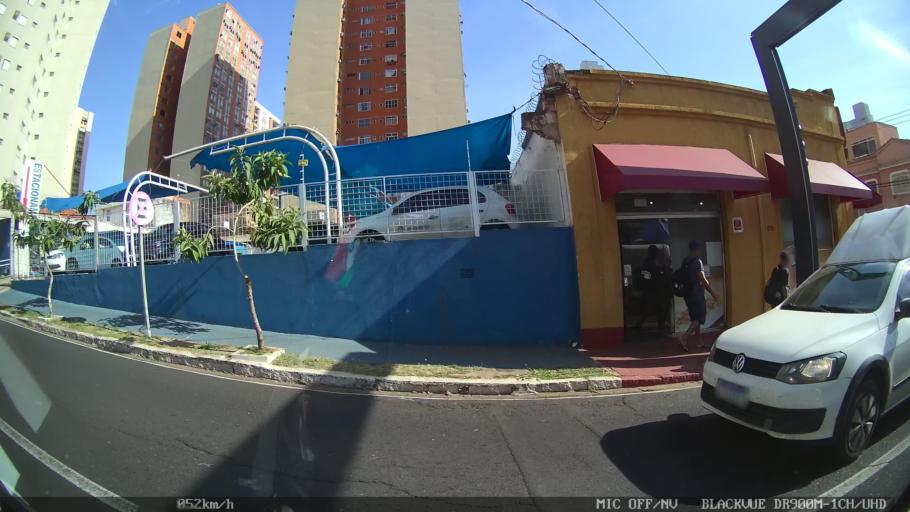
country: BR
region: Sao Paulo
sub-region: Sao Jose Do Rio Preto
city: Sao Jose do Rio Preto
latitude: -20.8131
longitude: -49.3871
